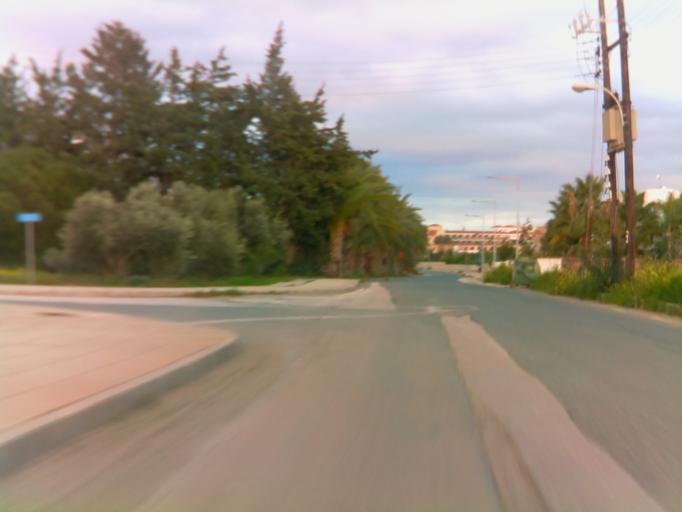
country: CY
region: Pafos
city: Pegeia
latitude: 34.8613
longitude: 32.3575
